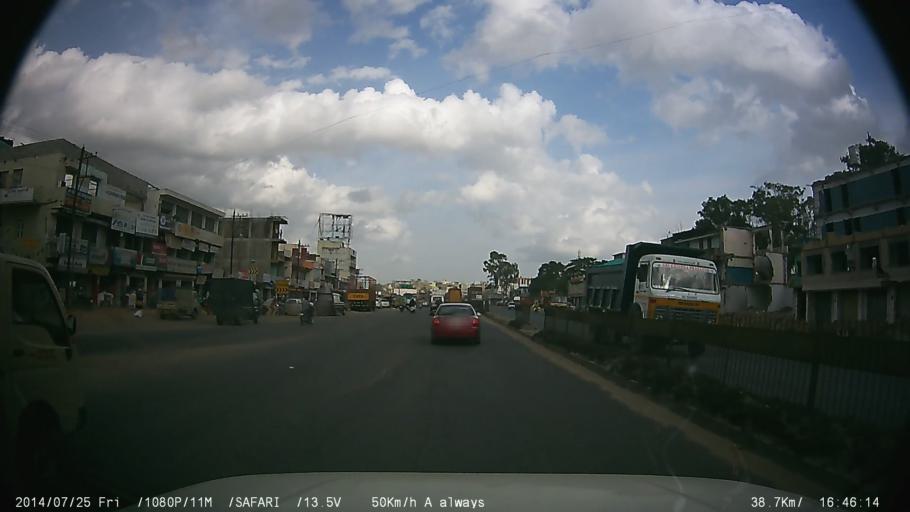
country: IN
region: Tamil Nadu
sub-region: Krishnagiri
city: Hosur
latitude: 12.7382
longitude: 77.8224
